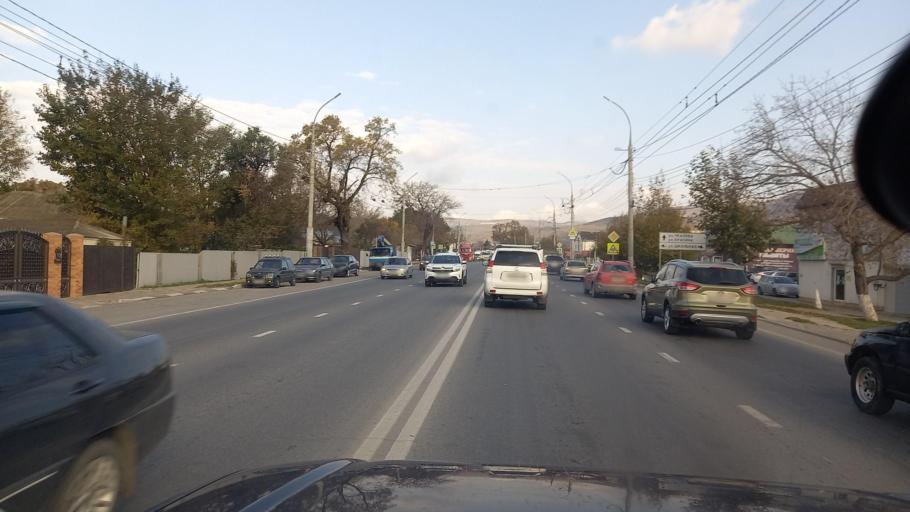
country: RU
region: Krasnodarskiy
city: Gayduk
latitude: 44.7538
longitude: 37.7266
